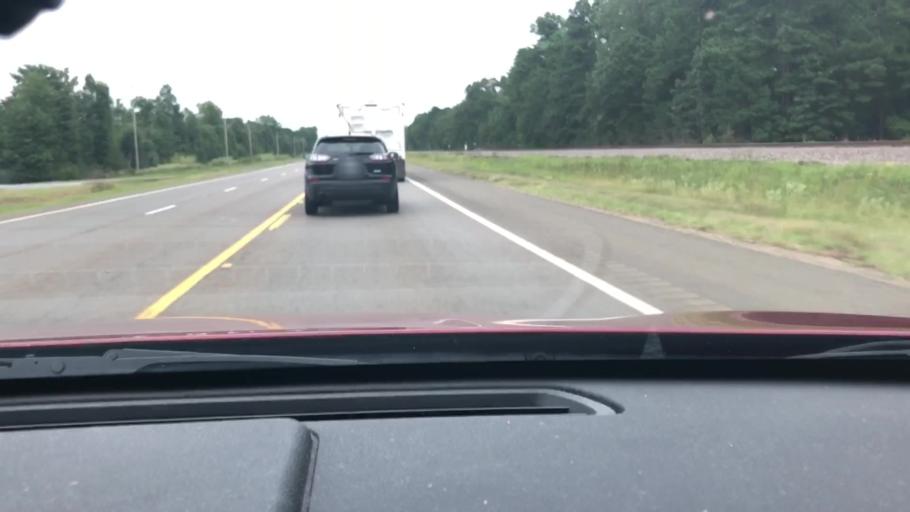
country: US
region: Arkansas
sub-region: Lafayette County
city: Lewisville
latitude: 33.3575
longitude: -93.5995
